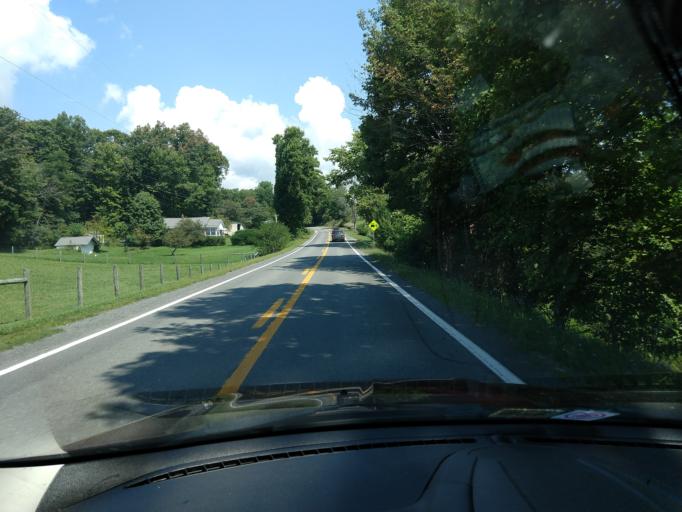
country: US
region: West Virginia
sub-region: Greenbrier County
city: Lewisburg
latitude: 37.8537
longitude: -80.5507
